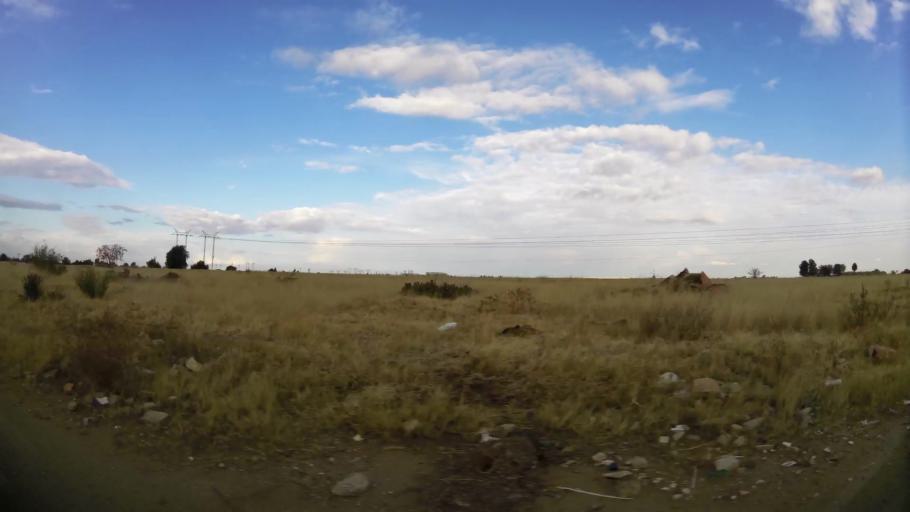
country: ZA
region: Orange Free State
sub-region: Lejweleputswa District Municipality
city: Welkom
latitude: -28.0065
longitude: 26.7317
